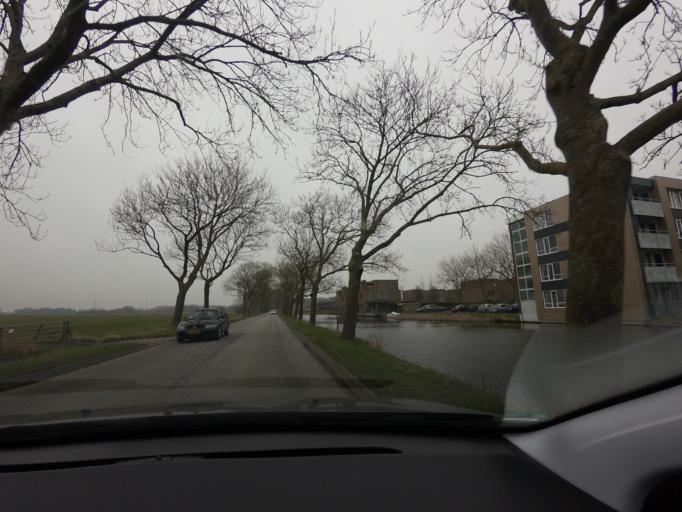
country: NL
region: Friesland
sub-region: Sudwest Fryslan
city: Bolsward
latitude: 53.0659
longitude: 5.5149
